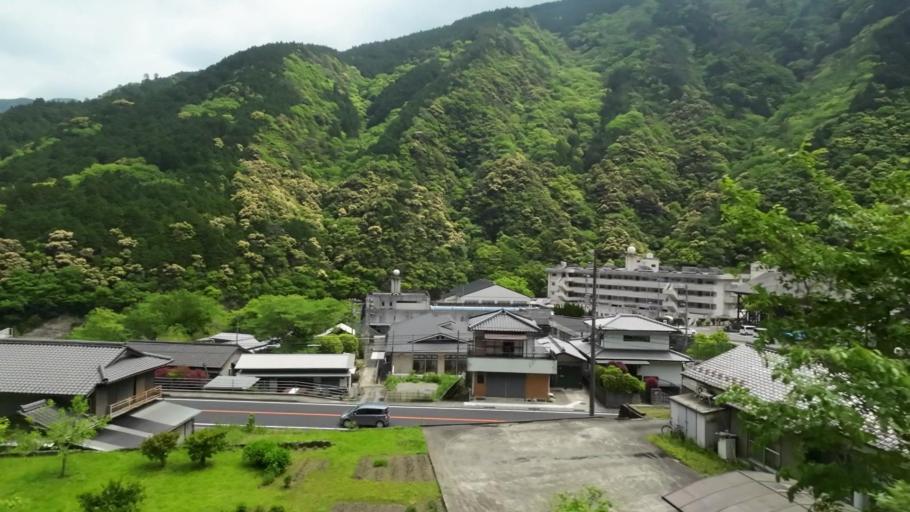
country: JP
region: Tokushima
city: Ikedacho
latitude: 33.9139
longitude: 133.7569
